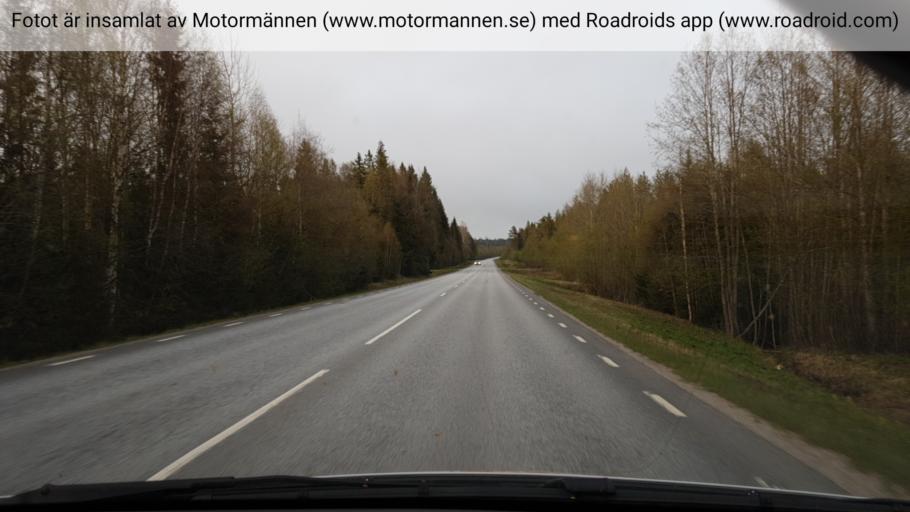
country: SE
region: Vaesterbotten
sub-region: Umea Kommun
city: Roback
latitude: 63.7806
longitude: 20.0802
